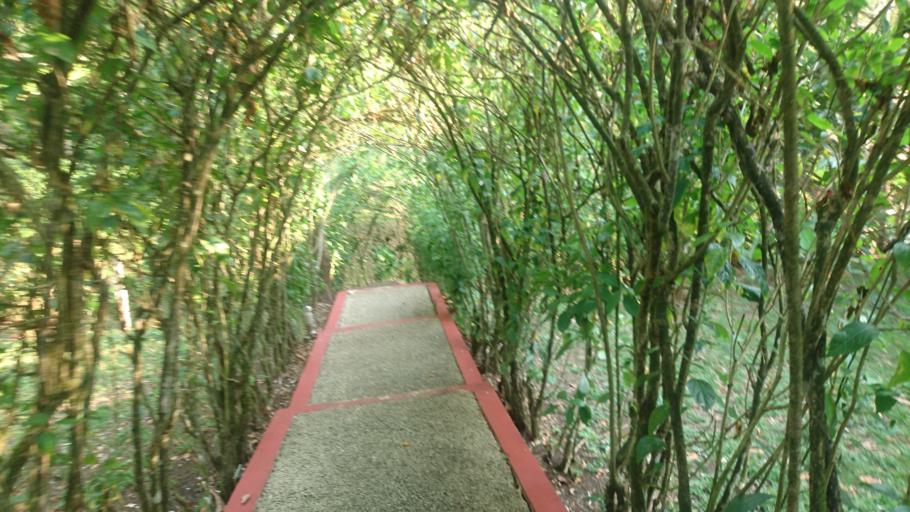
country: MX
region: Chiapas
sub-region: Marques de Comillas
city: Zamora Pico de Oro
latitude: 16.2573
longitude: -90.8617
